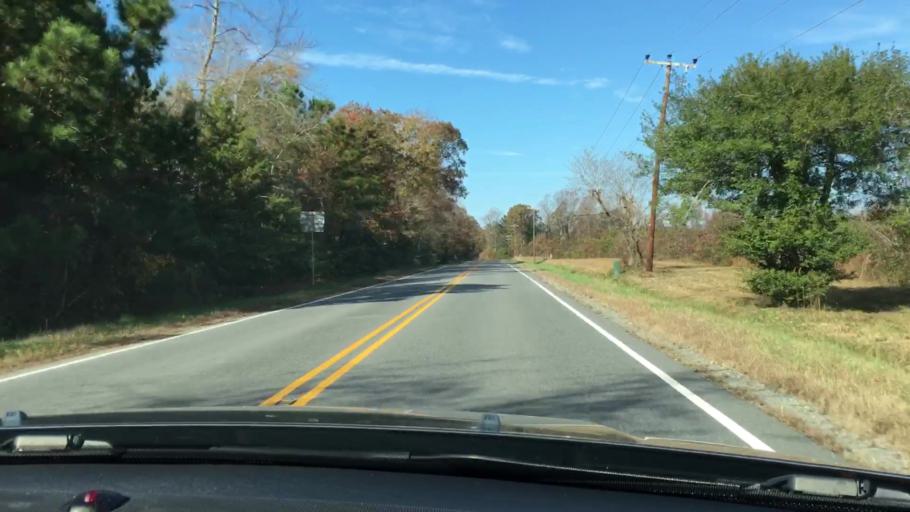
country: US
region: Virginia
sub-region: King and Queen County
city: King and Queen Court House
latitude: 37.6085
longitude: -76.9105
